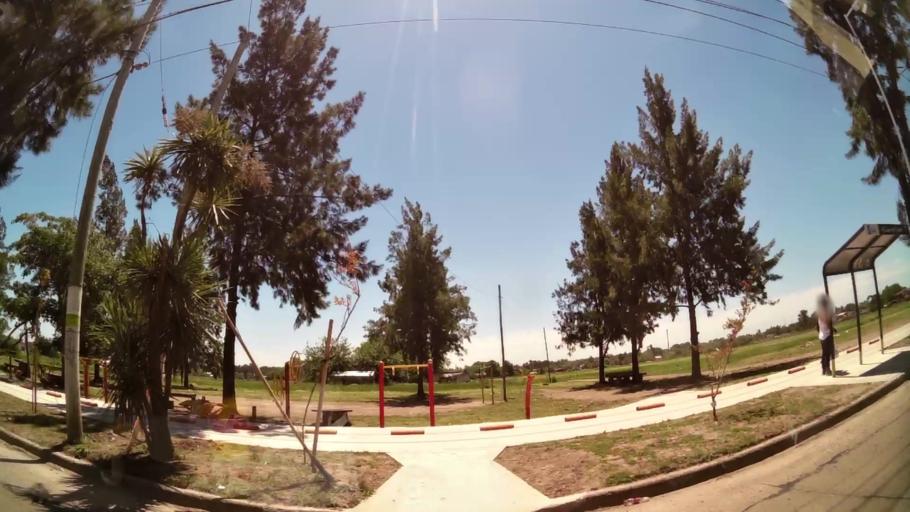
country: AR
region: Buenos Aires
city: Hurlingham
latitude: -34.4956
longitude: -58.6733
